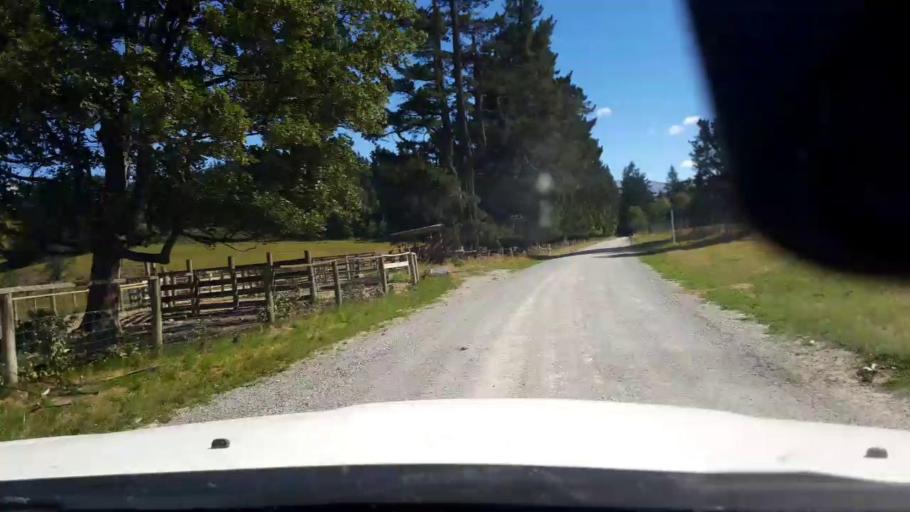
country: NZ
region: Canterbury
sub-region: Timaru District
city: Pleasant Point
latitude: -44.0290
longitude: 170.7435
